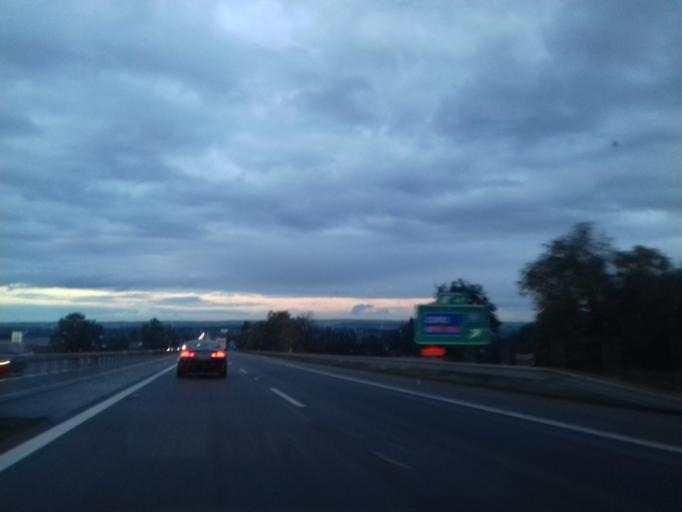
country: CZ
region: Central Bohemia
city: Cechtice
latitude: 49.6537
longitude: 15.1227
